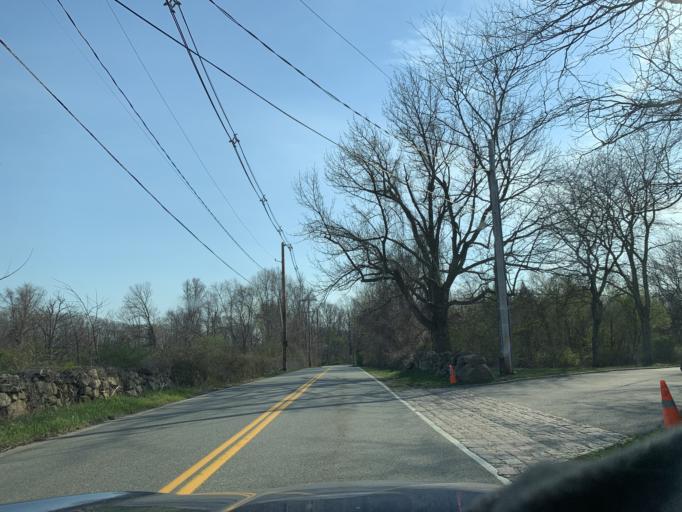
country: US
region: Rhode Island
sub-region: Kent County
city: West Warwick
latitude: 41.7415
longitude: -71.5330
